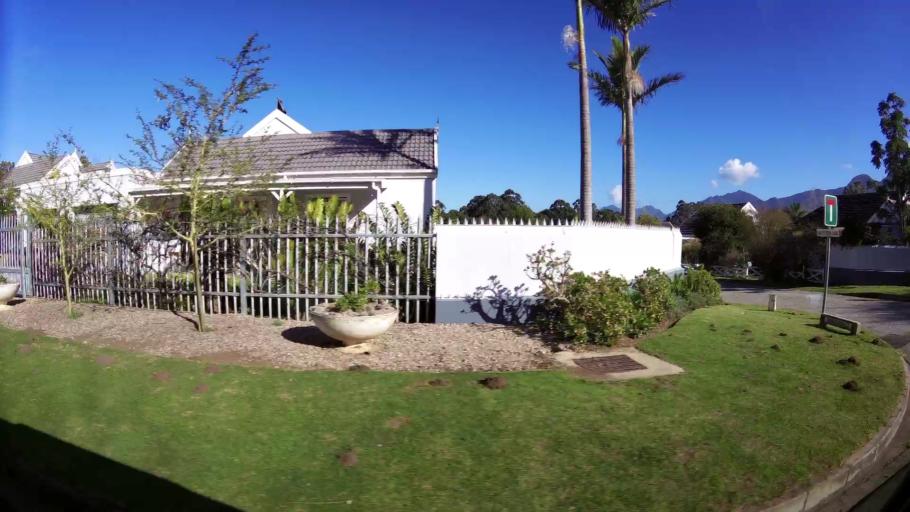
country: ZA
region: Western Cape
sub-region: Eden District Municipality
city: George
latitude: -33.9536
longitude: 22.4236
